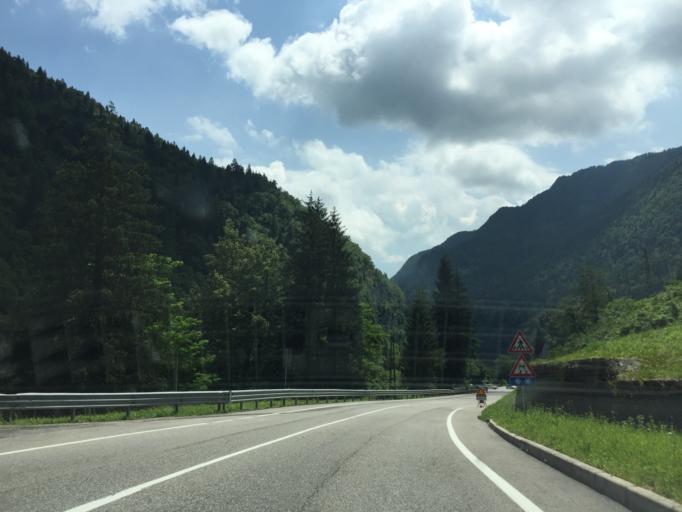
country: IT
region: Veneto
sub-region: Provincia di Belluno
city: Lamon
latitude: 46.0319
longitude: 11.7617
